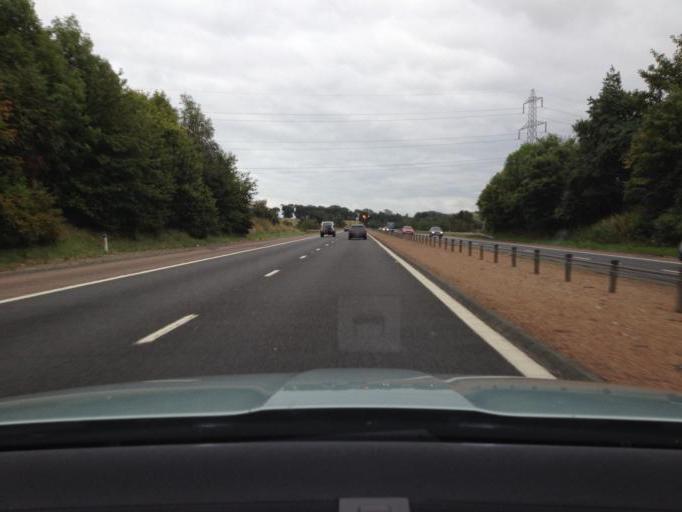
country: GB
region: Scotland
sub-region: Fife
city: Kelty
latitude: 56.1111
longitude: -3.3915
